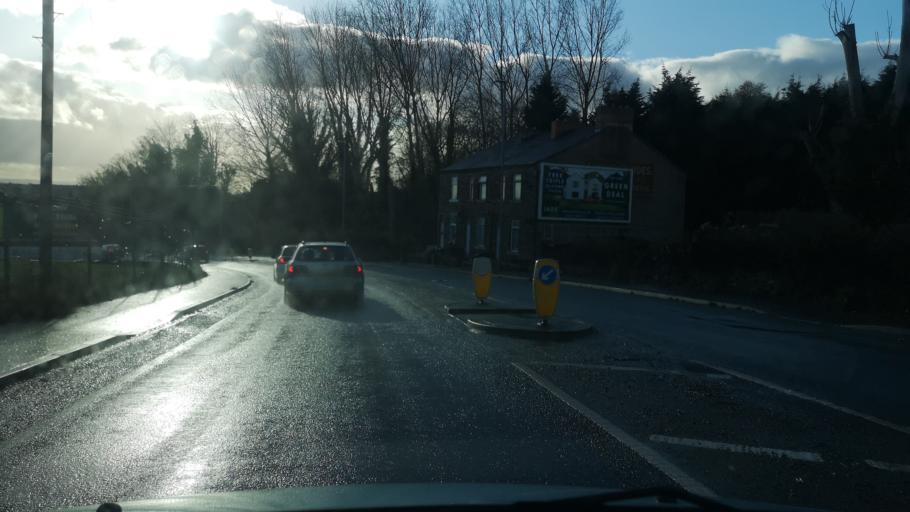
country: GB
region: England
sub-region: City and Borough of Leeds
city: Drighlington
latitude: 53.7358
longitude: -1.6567
